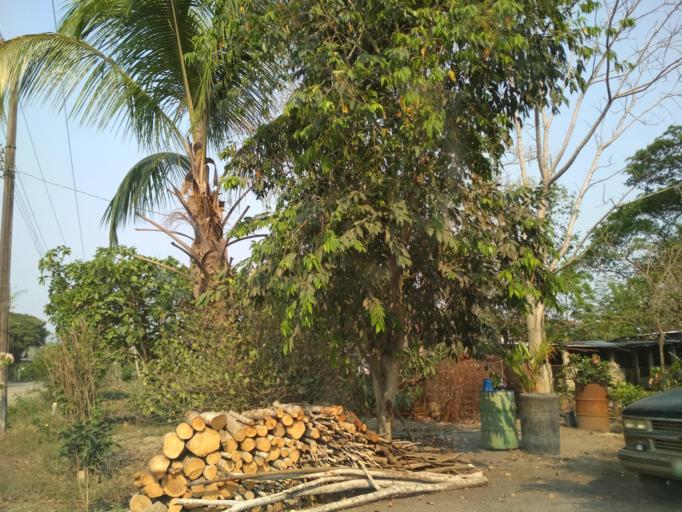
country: MX
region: Oaxaca
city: Acatlan de Perez Figueroa
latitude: 18.6068
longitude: -96.5747
